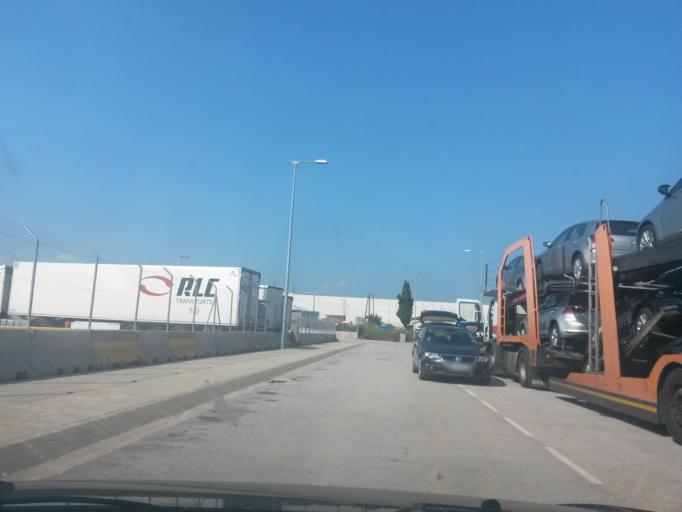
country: ES
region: Catalonia
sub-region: Provincia de Girona
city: Fornells de la Selva
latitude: 41.9371
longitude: 2.7987
